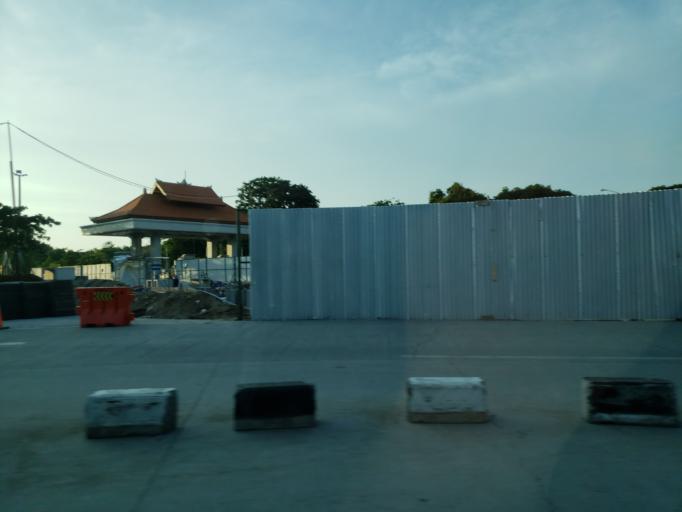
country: ID
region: Bali
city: Kelanabian
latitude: -8.7410
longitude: 115.1648
